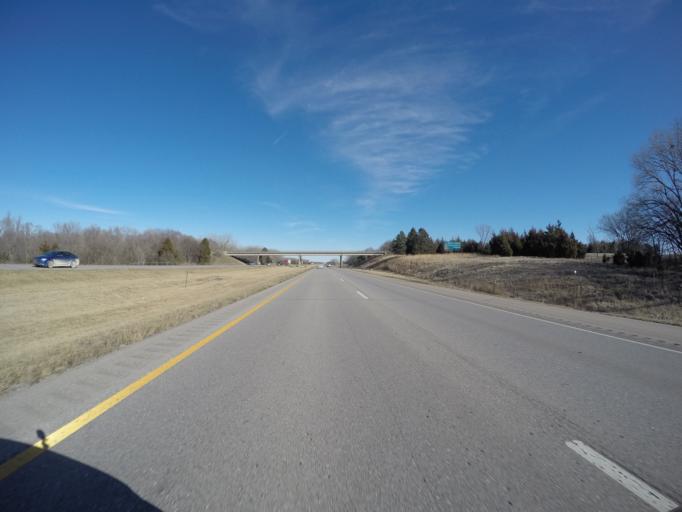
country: US
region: Nebraska
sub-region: Seward County
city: Milford
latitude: 40.8203
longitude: -96.8939
